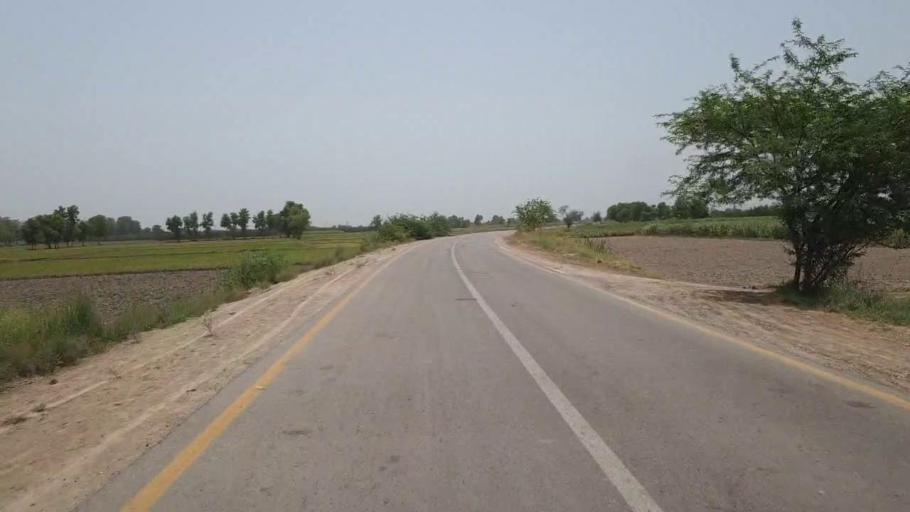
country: PK
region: Sindh
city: Moro
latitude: 26.6026
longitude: 68.0588
